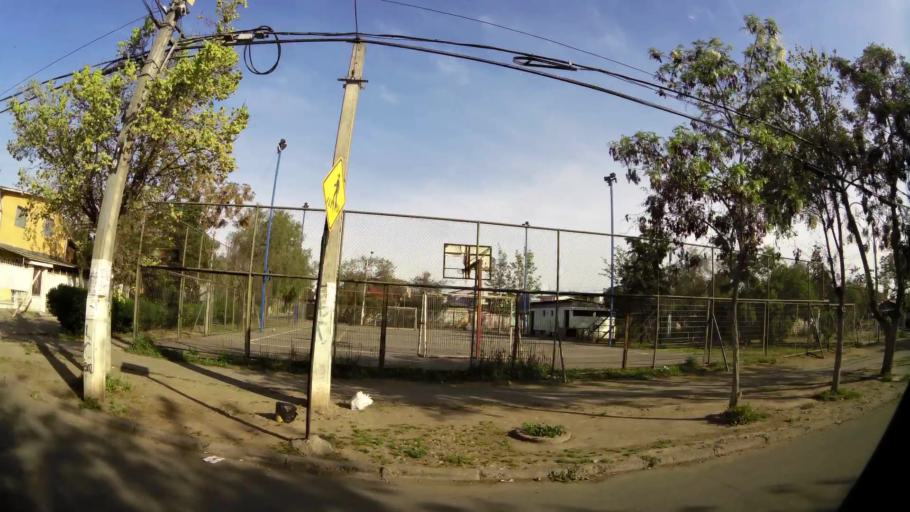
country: CL
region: Santiago Metropolitan
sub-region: Provincia de Santiago
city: Santiago
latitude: -33.5101
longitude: -70.6315
